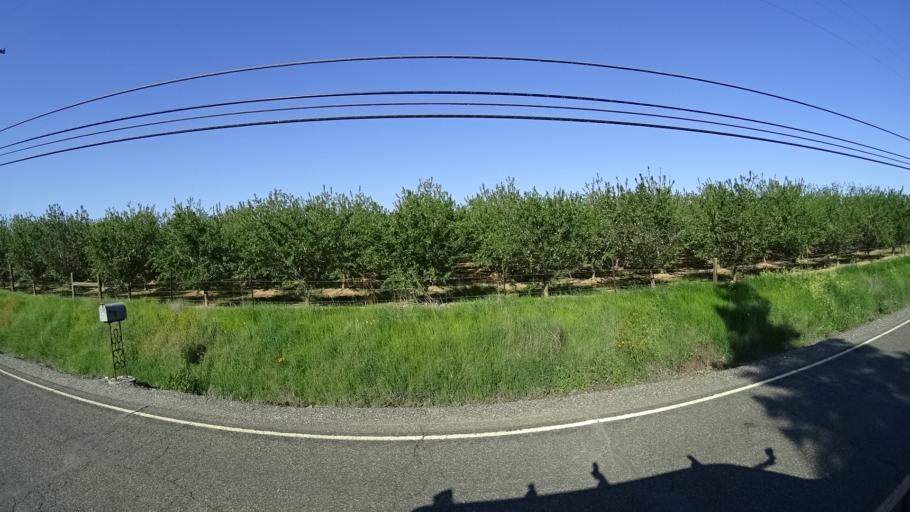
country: US
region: California
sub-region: Glenn County
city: Orland
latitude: 39.7806
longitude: -122.1041
